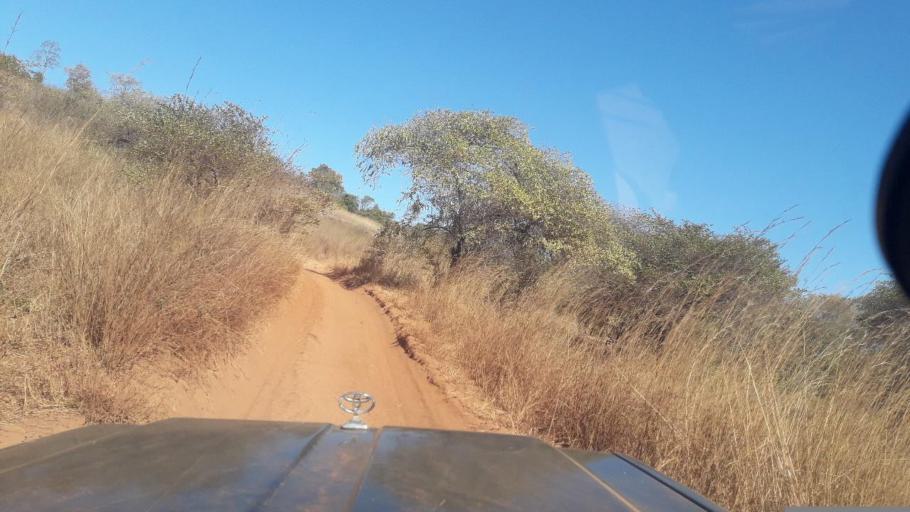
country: MG
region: Boeny
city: Sitampiky
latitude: -16.3112
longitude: 45.6300
